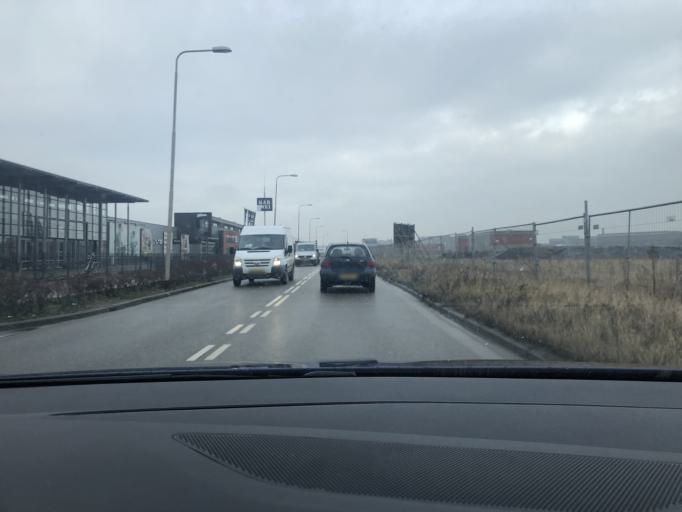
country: NL
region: South Holland
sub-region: Gemeente Hendrik-Ido-Ambacht
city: Hendrik-Ido-Ambacht
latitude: 51.8453
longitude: 4.6572
